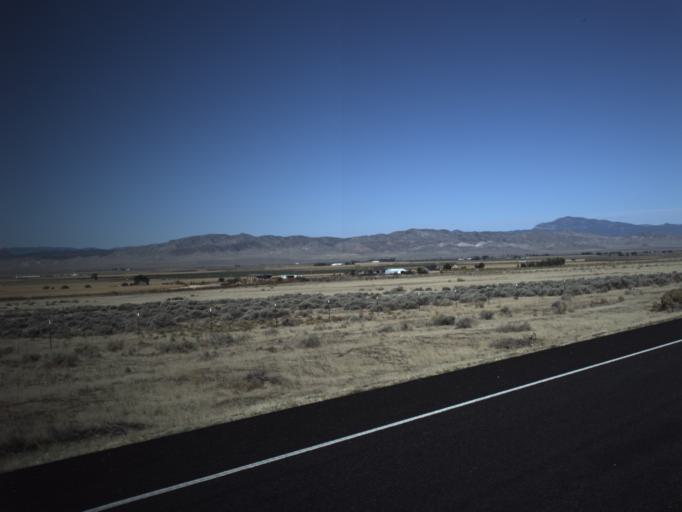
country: US
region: Utah
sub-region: Beaver County
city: Milford
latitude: 38.2743
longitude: -112.9597
